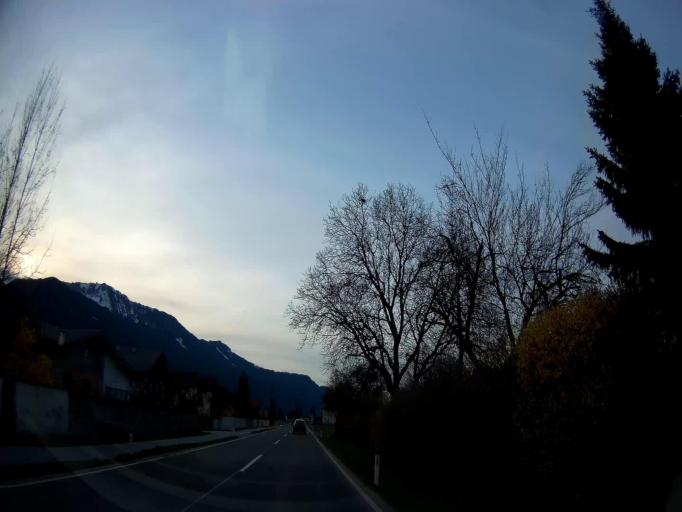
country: AT
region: Salzburg
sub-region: Politischer Bezirk Hallein
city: Kuchl
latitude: 47.6181
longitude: 13.1596
